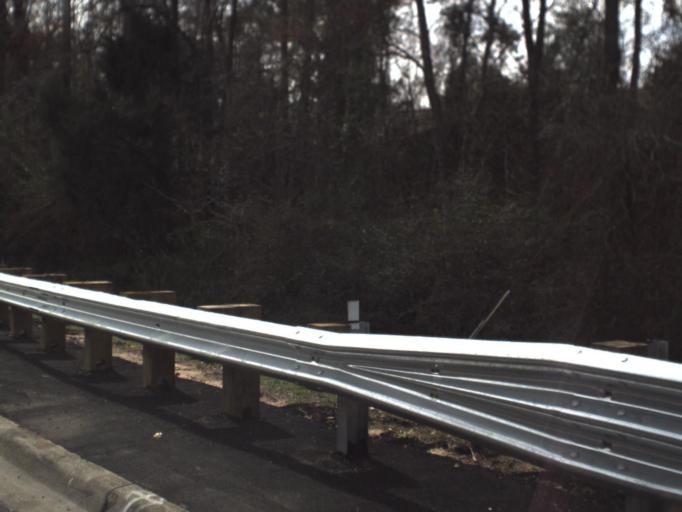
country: US
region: Florida
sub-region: Washington County
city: Chipley
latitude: 30.6896
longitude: -85.3928
